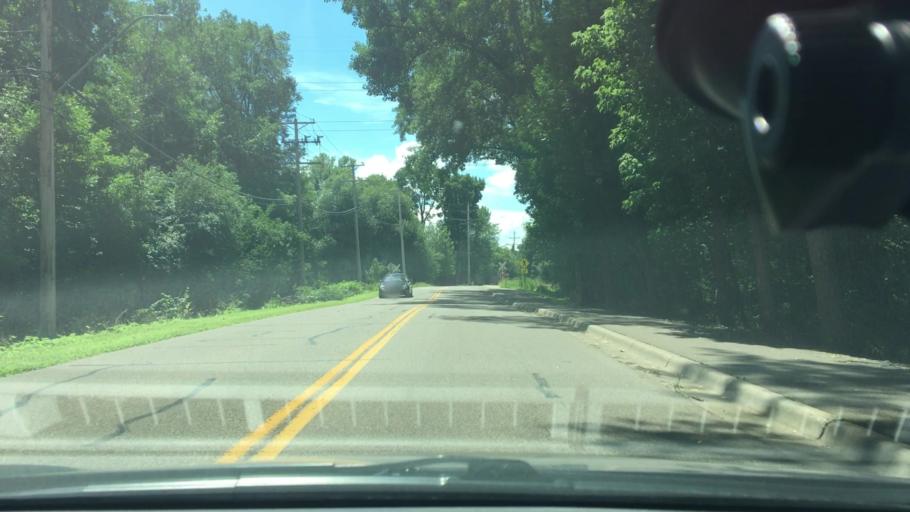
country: US
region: Minnesota
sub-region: Hennepin County
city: Plymouth
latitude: 44.9941
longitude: -93.4170
